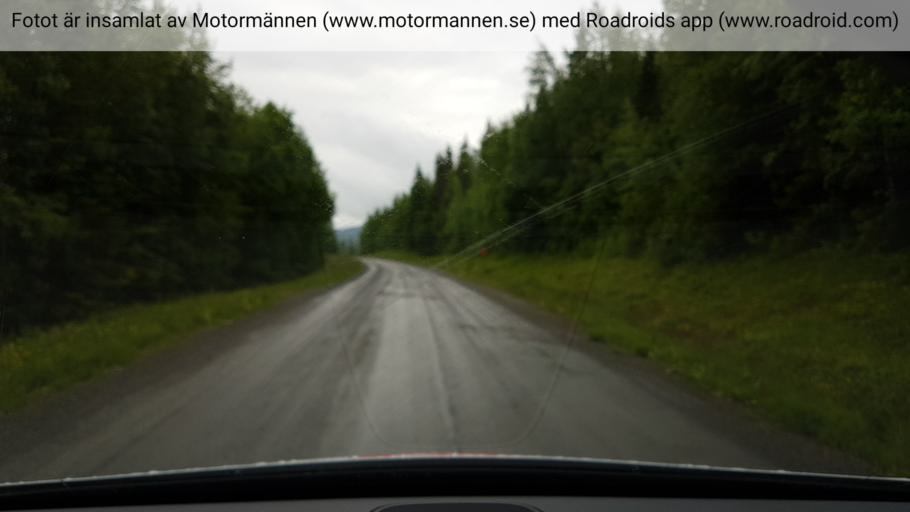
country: SE
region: Jaemtland
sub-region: Stroemsunds Kommun
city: Stroemsund
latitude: 64.2889
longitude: 15.0049
